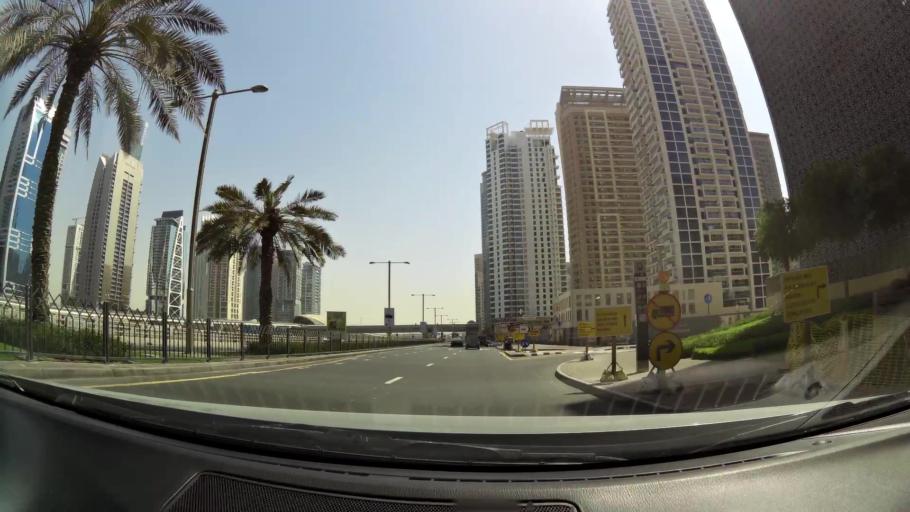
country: AE
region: Dubai
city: Dubai
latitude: 25.0748
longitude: 55.1402
